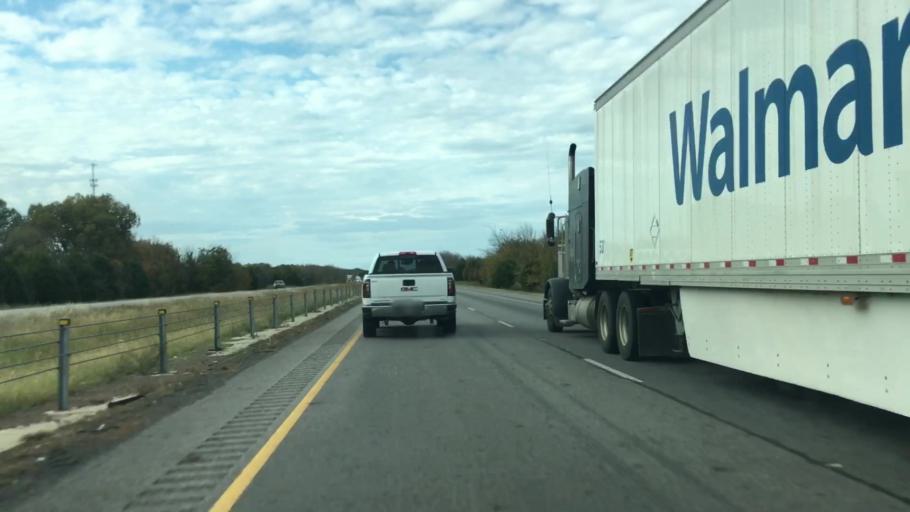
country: US
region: Arkansas
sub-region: Conway County
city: Morrilton
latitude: 35.2027
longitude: -92.8084
